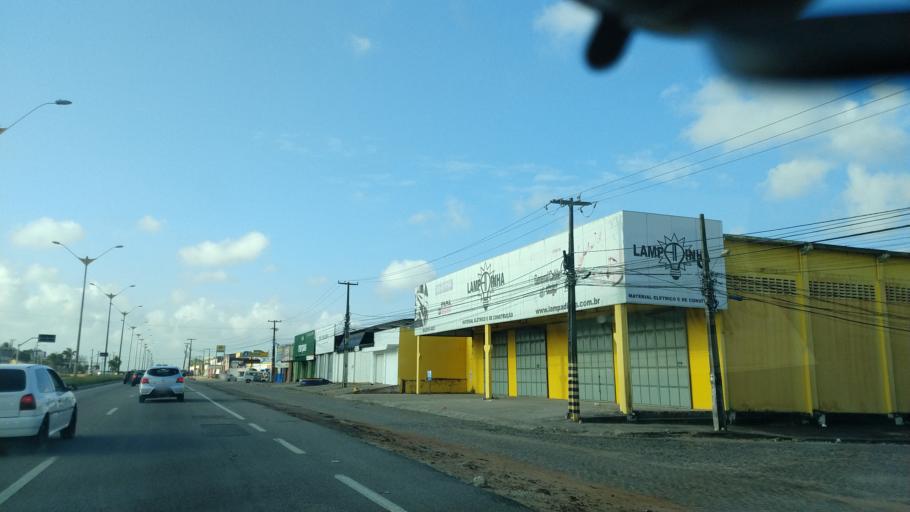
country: BR
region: Rio Grande do Norte
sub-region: Parnamirim
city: Parnamirim
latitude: -5.8988
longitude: -35.2587
